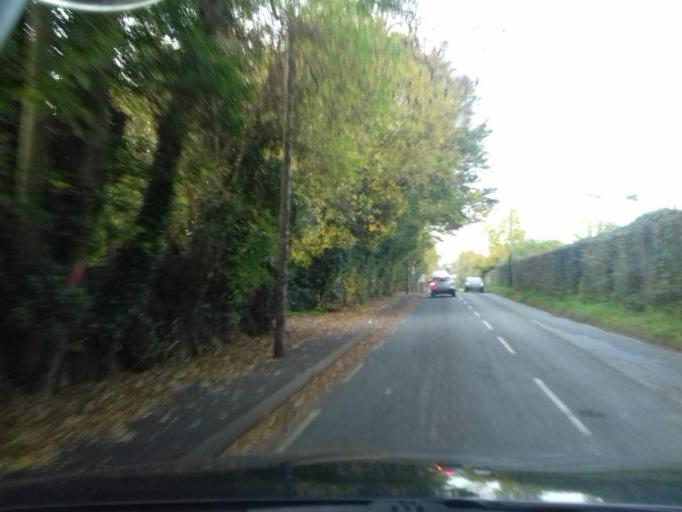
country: IE
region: Leinster
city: Hartstown
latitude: 53.3809
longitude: -6.4224
